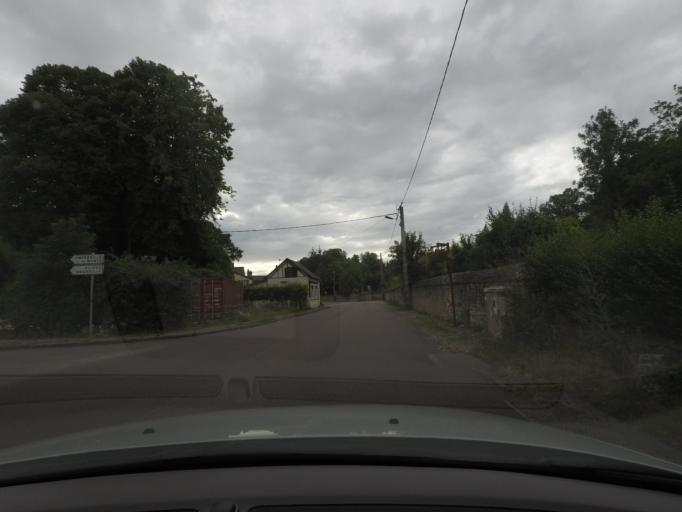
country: FR
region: Haute-Normandie
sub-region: Departement de l'Eure
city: Pont-Saint-Pierre
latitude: 49.3317
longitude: 1.2856
